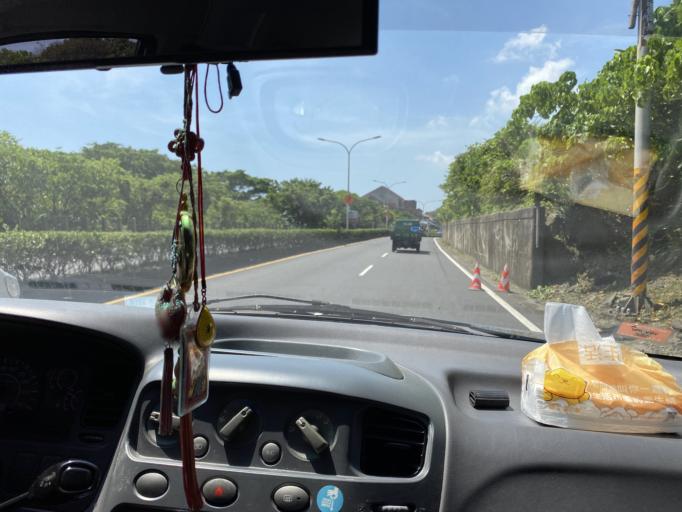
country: TW
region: Taiwan
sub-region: Yilan
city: Yilan
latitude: 24.9167
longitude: 121.8821
